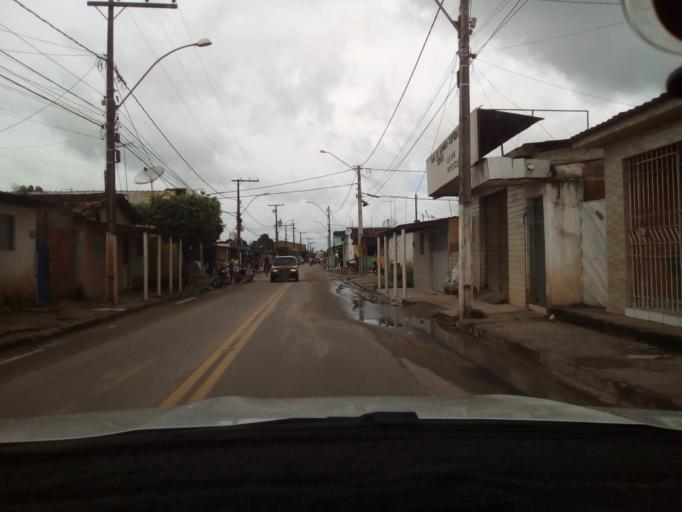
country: BR
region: Paraiba
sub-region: Pedras De Fogo
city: Pedras de Fogo
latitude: -7.4043
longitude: -35.1073
